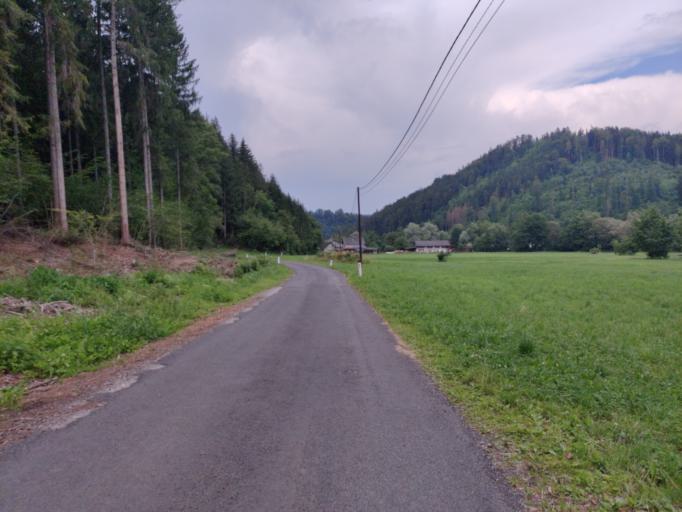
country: AT
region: Styria
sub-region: Politischer Bezirk Graz-Umgebung
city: Gratwein
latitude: 47.1147
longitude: 15.2963
